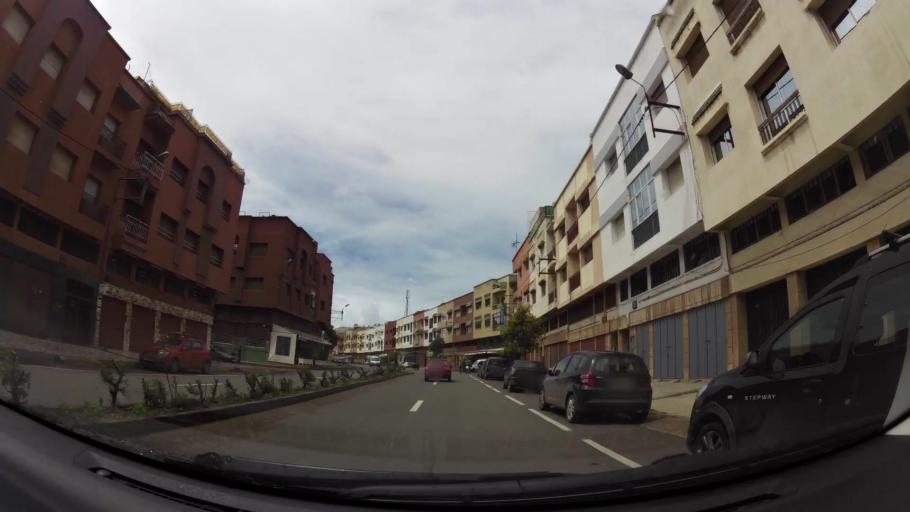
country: MA
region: Grand Casablanca
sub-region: Casablanca
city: Casablanca
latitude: 33.5490
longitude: -7.6858
